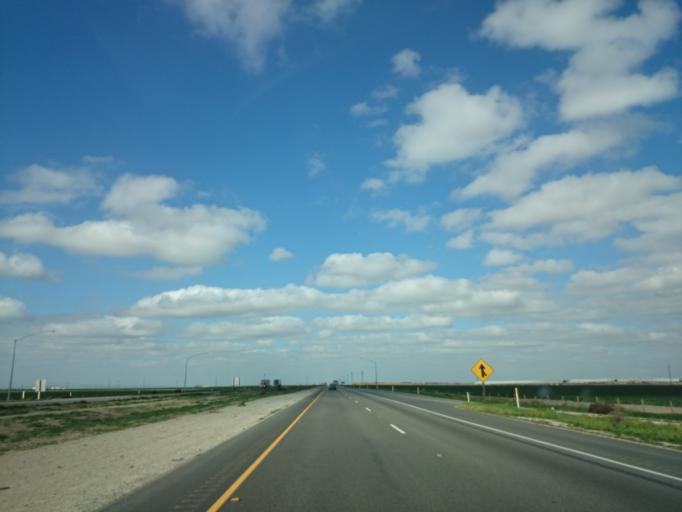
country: US
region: California
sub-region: Kern County
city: Greenfield
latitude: 35.1631
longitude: -119.1123
